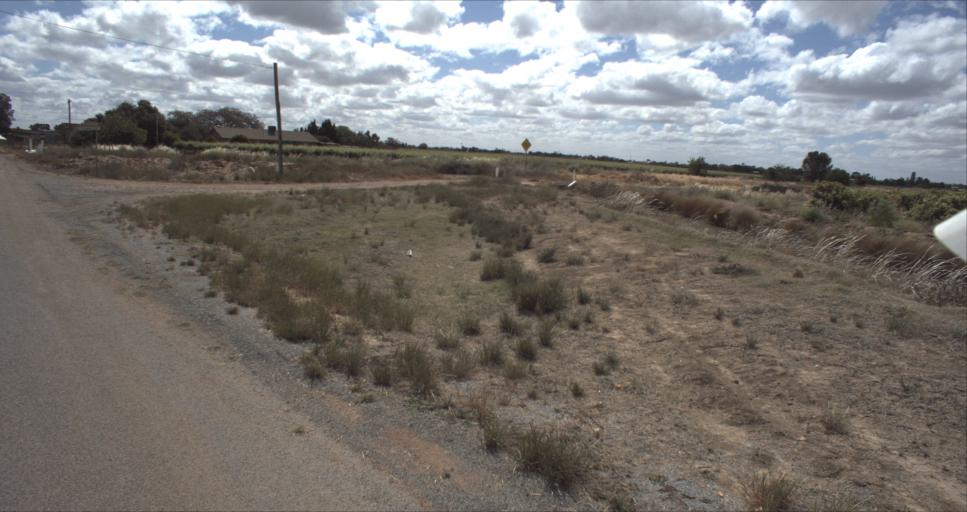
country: AU
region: New South Wales
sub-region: Leeton
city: Leeton
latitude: -34.5802
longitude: 146.3927
